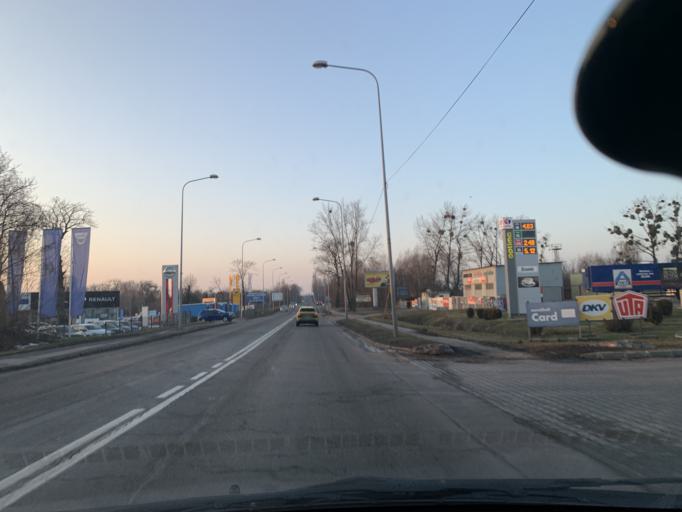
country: PL
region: Silesian Voivodeship
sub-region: Piekary Slaskie
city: Piekary Slaskie
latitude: 50.3596
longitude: 18.9053
